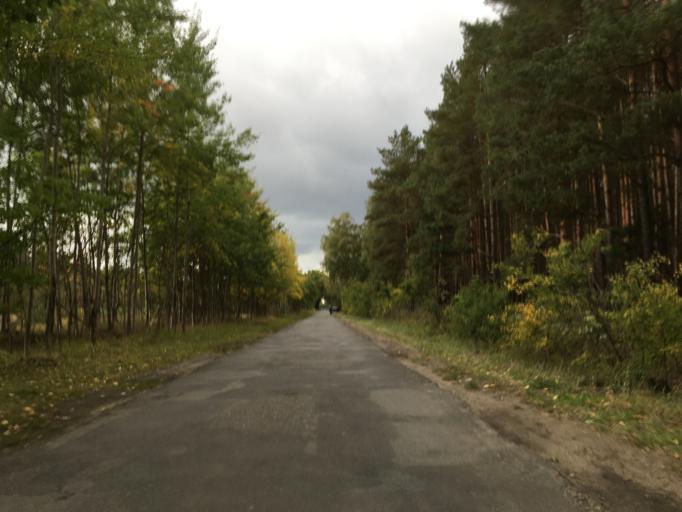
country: DE
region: Brandenburg
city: Birkenwerder
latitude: 52.6932
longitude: 13.3295
